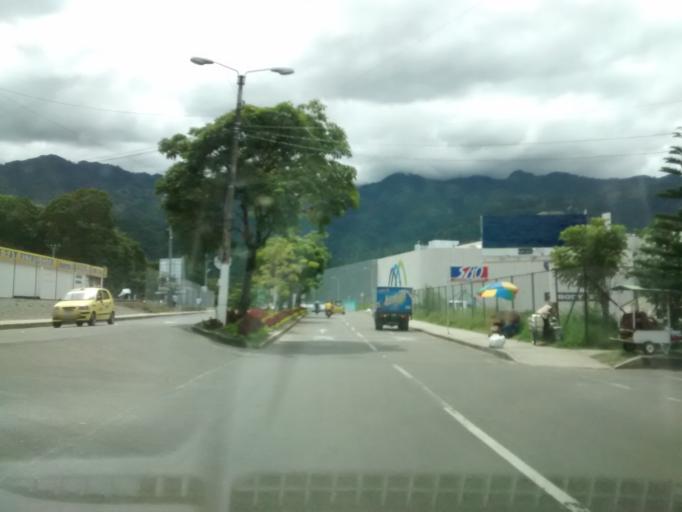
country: CO
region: Tolima
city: Ibague
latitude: 4.4436
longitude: -75.2049
